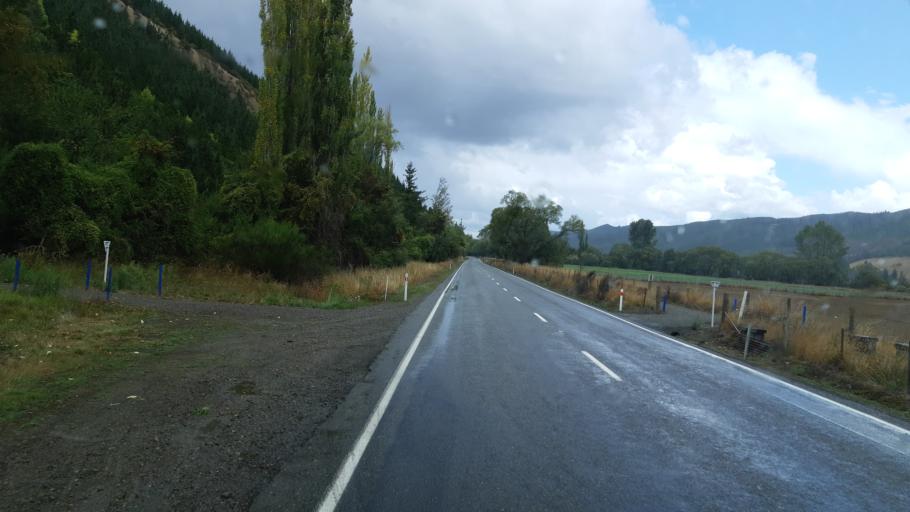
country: NZ
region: Tasman
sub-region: Tasman District
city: Wakefield
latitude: -41.4623
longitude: 172.8391
